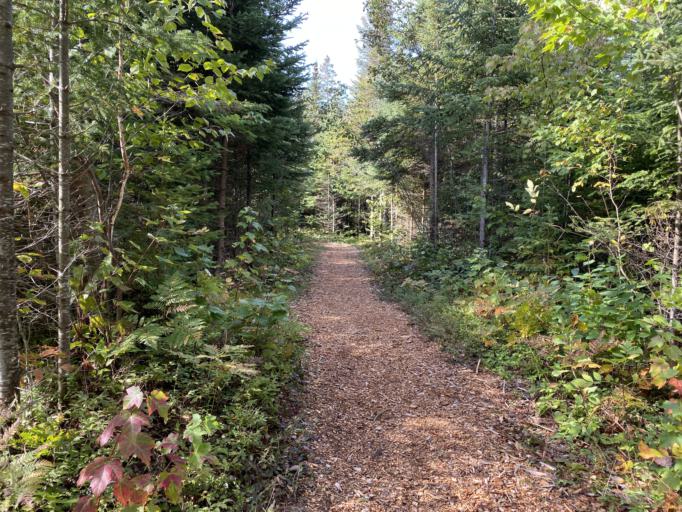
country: US
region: Michigan
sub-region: Mackinac County
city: Saint Ignace
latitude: 45.7444
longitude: -84.8950
